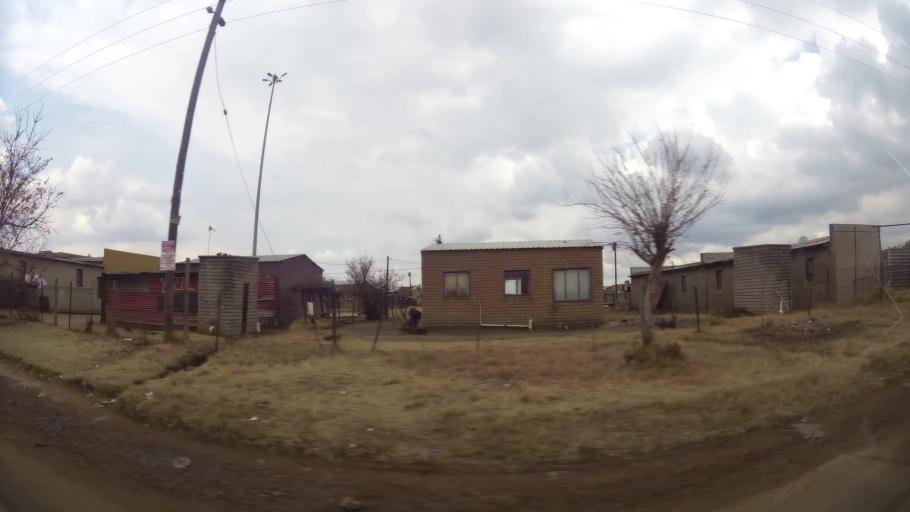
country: ZA
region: Orange Free State
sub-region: Fezile Dabi District Municipality
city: Sasolburg
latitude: -26.8561
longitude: 27.8853
